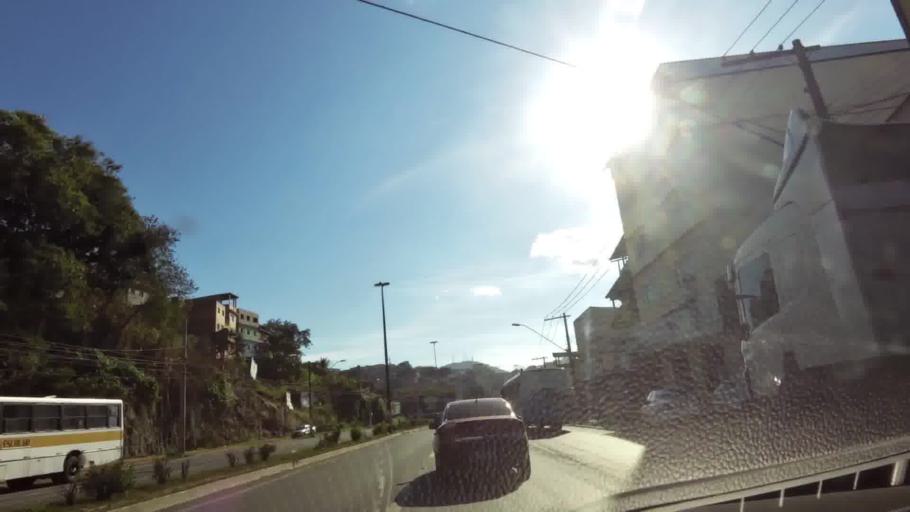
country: BR
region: Espirito Santo
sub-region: Vitoria
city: Vitoria
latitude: -20.3326
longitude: -40.3677
